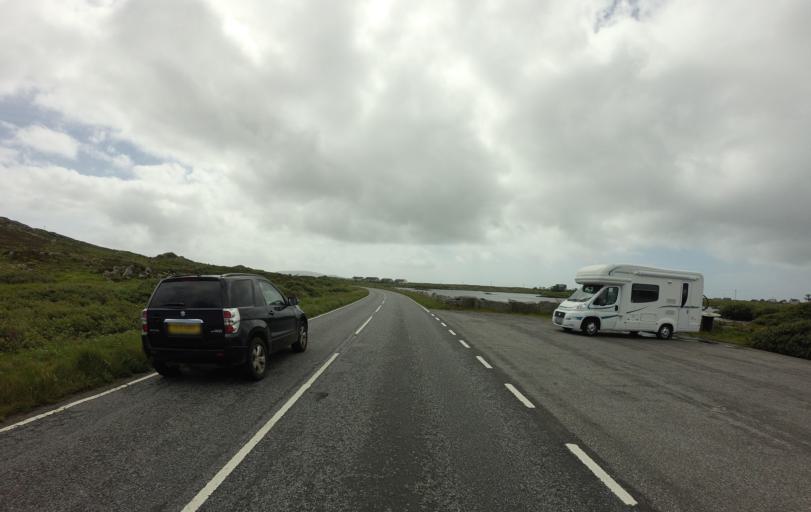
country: GB
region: Scotland
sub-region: Eilean Siar
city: Isle of South Uist
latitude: 57.1904
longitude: -7.3885
